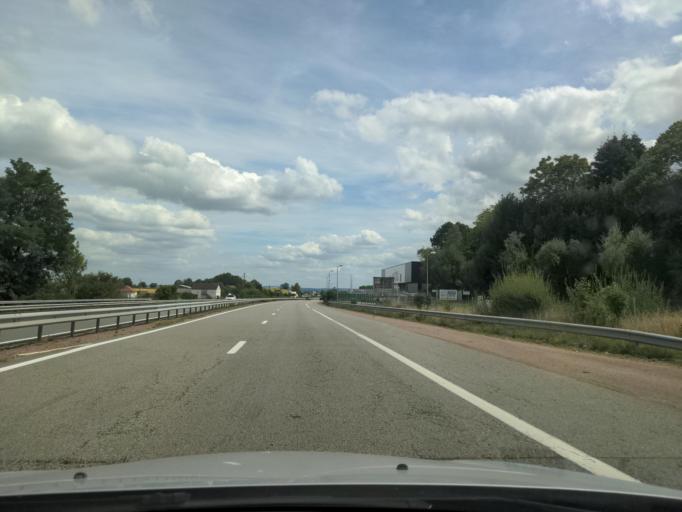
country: FR
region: Limousin
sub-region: Departement de la Creuse
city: Saint-Sulpice-le-Gueretois
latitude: 46.1863
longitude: 1.8270
